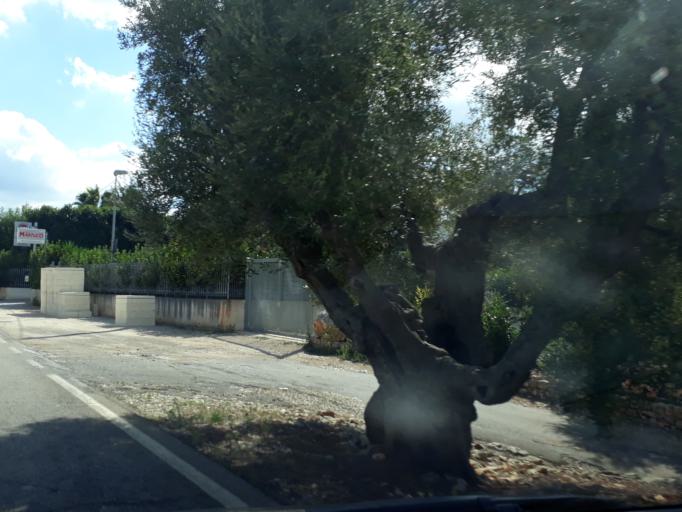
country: IT
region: Apulia
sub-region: Provincia di Brindisi
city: Fasano
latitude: 40.8229
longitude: 17.3734
